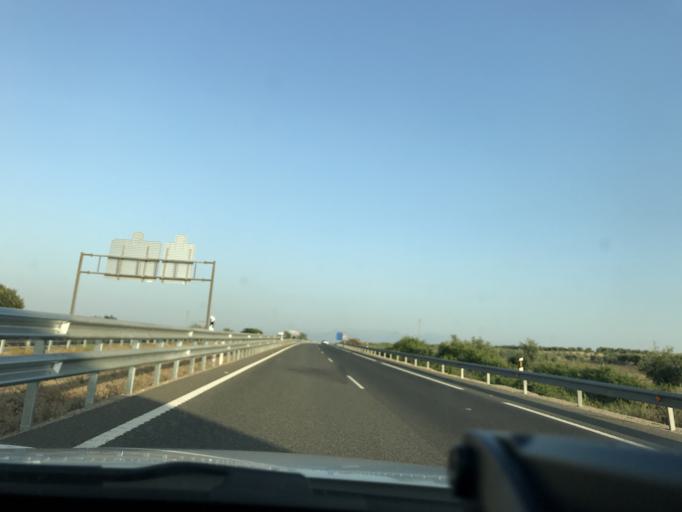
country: ES
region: Andalusia
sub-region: Provincia de Jaen
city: Bailen
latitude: 38.1123
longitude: -3.7504
